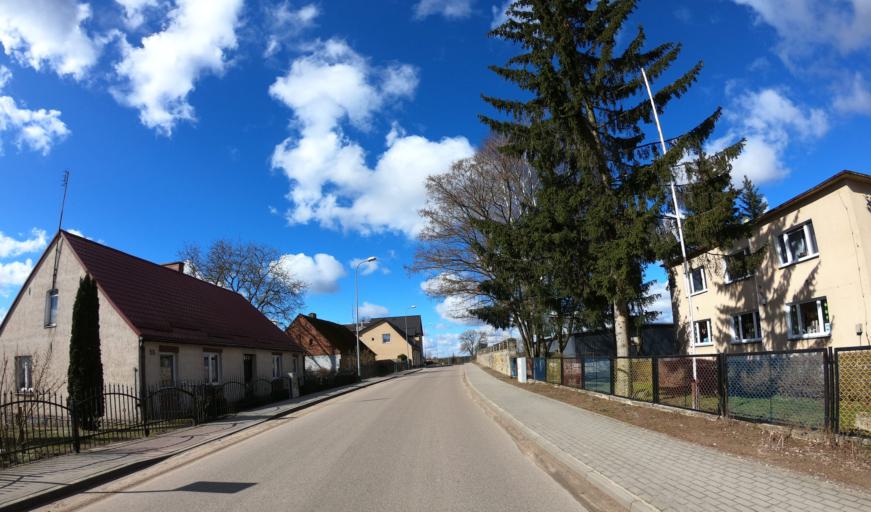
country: PL
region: West Pomeranian Voivodeship
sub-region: Powiat drawski
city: Drawsko Pomorskie
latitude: 53.4933
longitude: 15.8564
